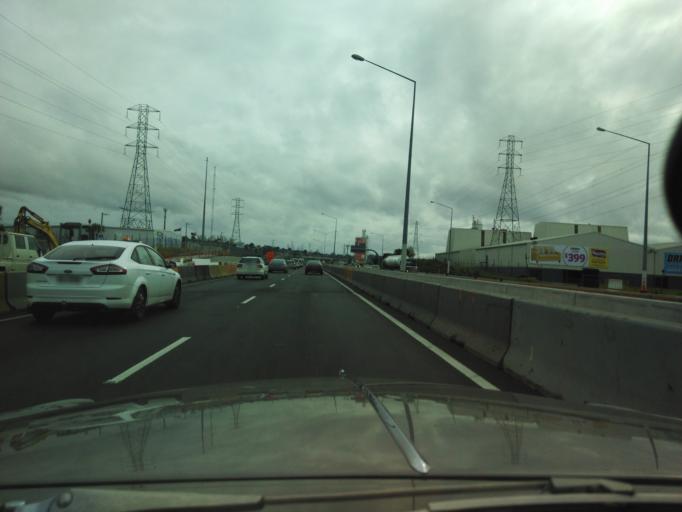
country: NZ
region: Auckland
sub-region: Auckland
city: Rosebank
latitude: -36.8527
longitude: 174.6405
